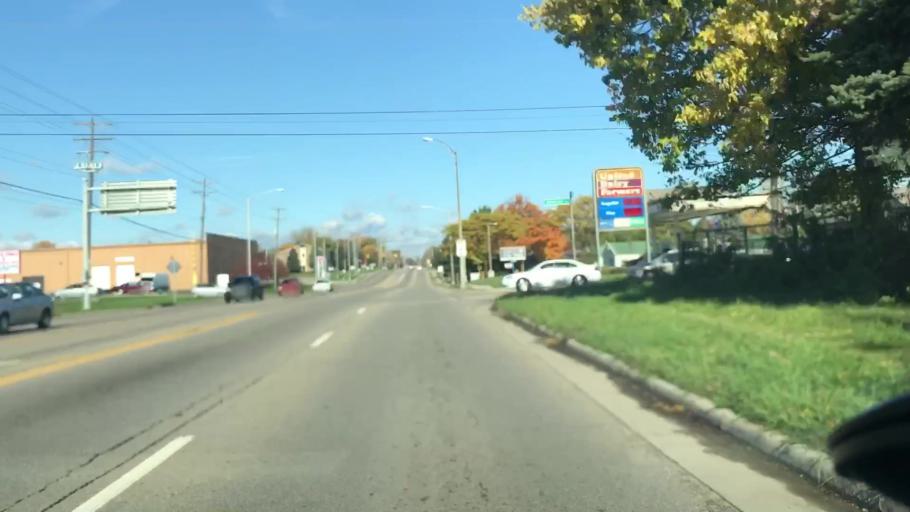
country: US
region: Ohio
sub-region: Franklin County
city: Lincoln Village
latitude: 39.9771
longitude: -83.1012
